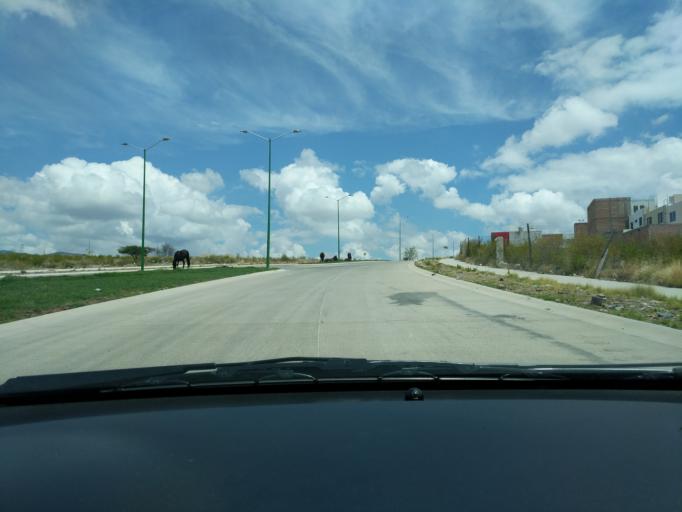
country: MX
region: San Luis Potosi
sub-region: Mexquitic de Carmona
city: Guadalupe Victoria
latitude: 22.1553
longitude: -101.0519
